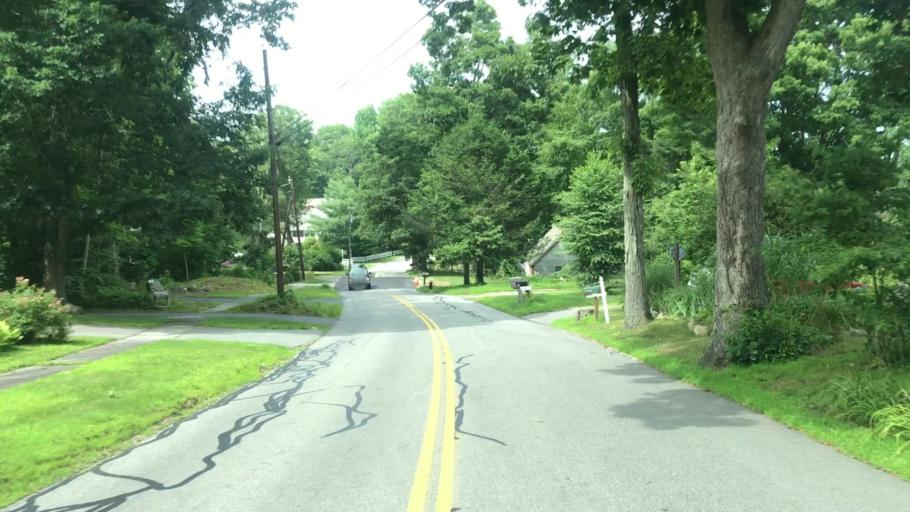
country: US
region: Connecticut
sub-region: New London County
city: Niantic
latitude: 41.3406
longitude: -72.2165
